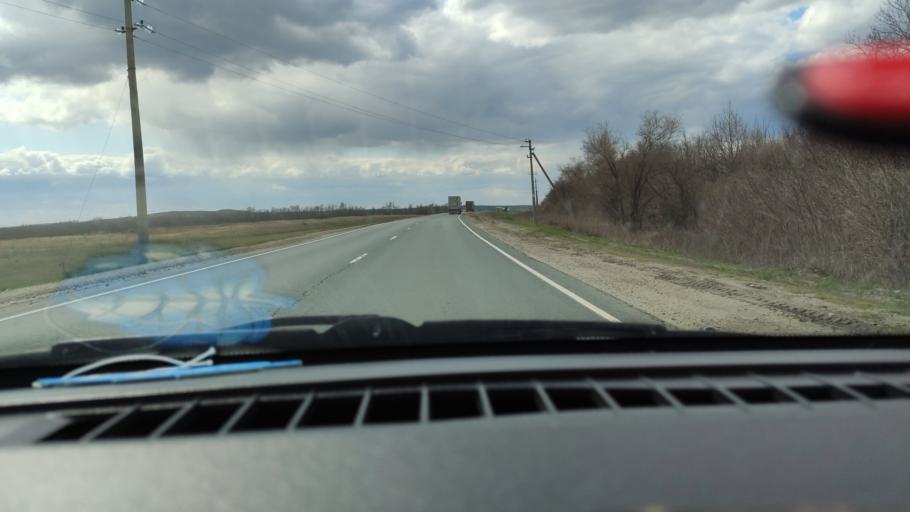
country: RU
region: Saratov
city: Alekseyevka
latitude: 52.2660
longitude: 47.9251
